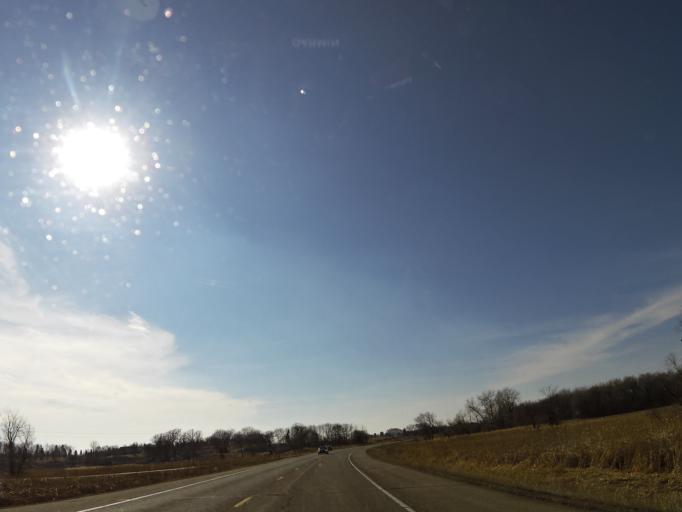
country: US
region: Minnesota
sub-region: Scott County
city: Prior Lake
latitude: 44.6894
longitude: -93.4730
